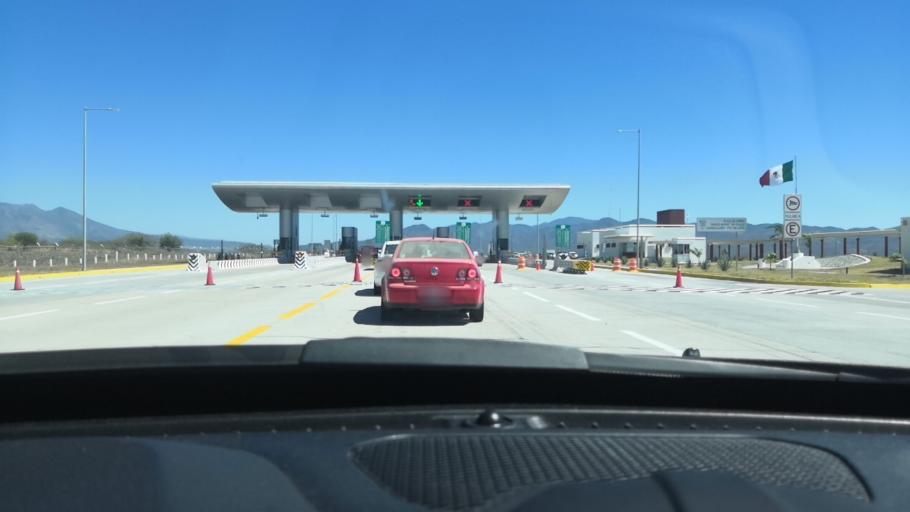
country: MX
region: Nayarit
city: San Pedro Lagunillas
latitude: 21.0964
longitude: -104.7603
